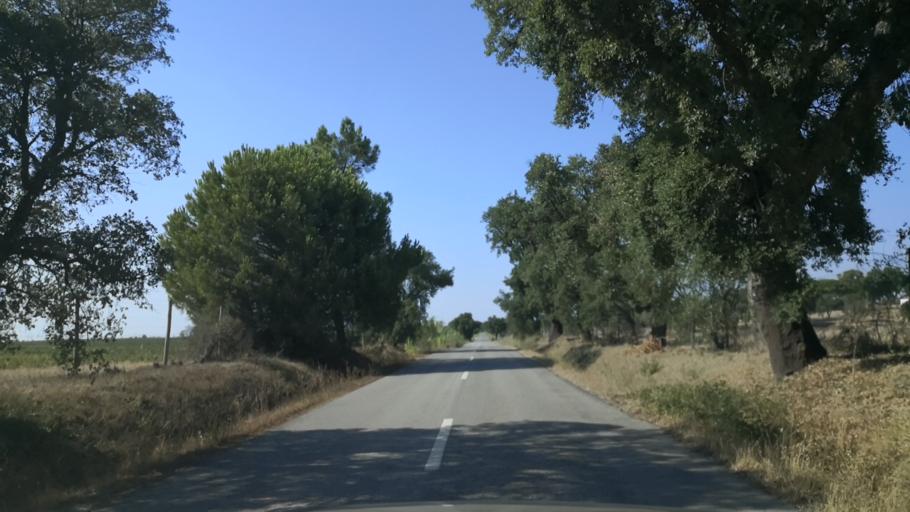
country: PT
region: Evora
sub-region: Vendas Novas
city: Vendas Novas
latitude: 38.7318
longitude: -8.6237
